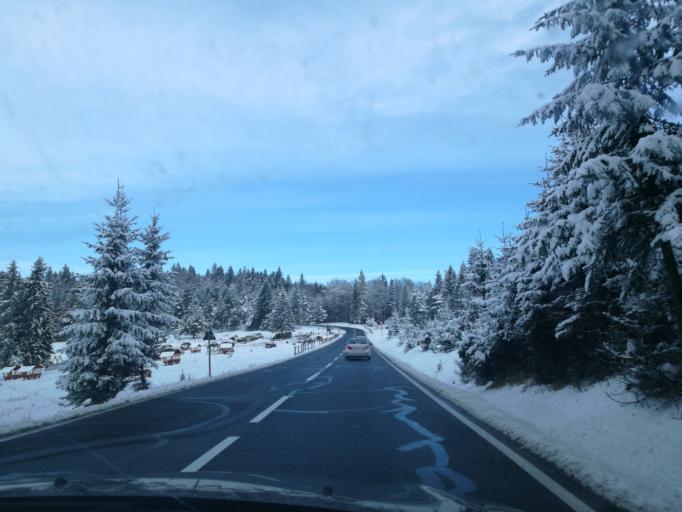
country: RO
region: Brasov
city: Brasov
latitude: 45.6141
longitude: 25.5467
